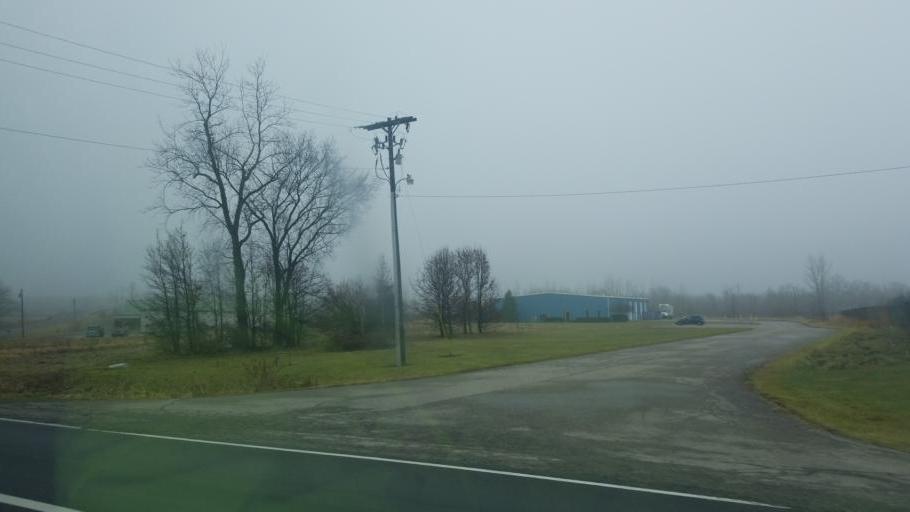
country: US
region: Ohio
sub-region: Union County
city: Marysville
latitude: 40.2610
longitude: -83.4606
